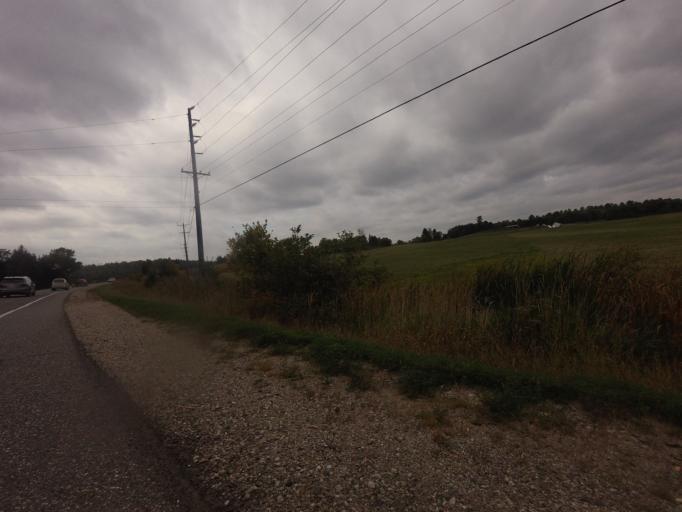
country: CA
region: Quebec
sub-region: Outaouais
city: Wakefield
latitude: 45.9118
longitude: -76.0174
